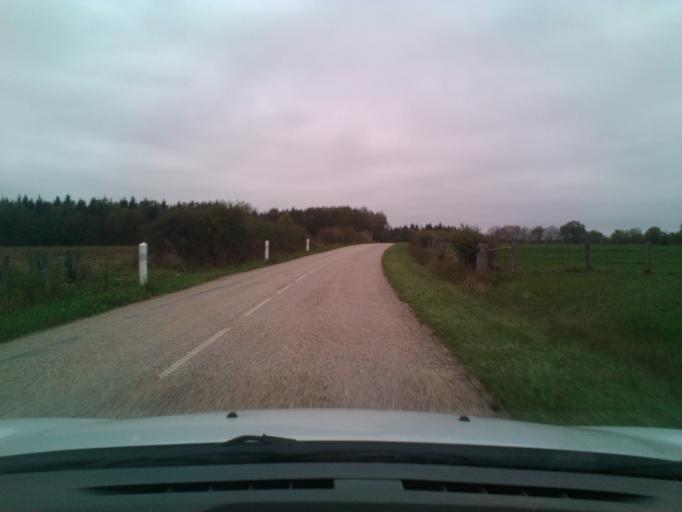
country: FR
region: Lorraine
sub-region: Departement des Vosges
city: Chavelot
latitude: 48.2826
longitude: 6.4612
